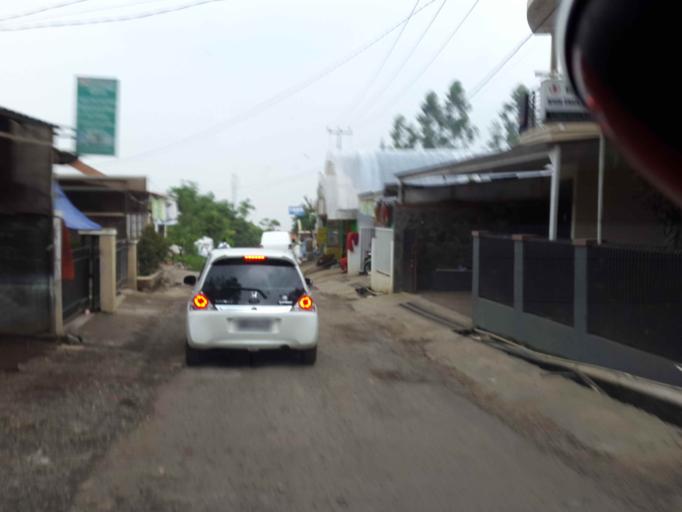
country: ID
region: West Java
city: Lembang
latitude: -6.8363
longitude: 107.5855
